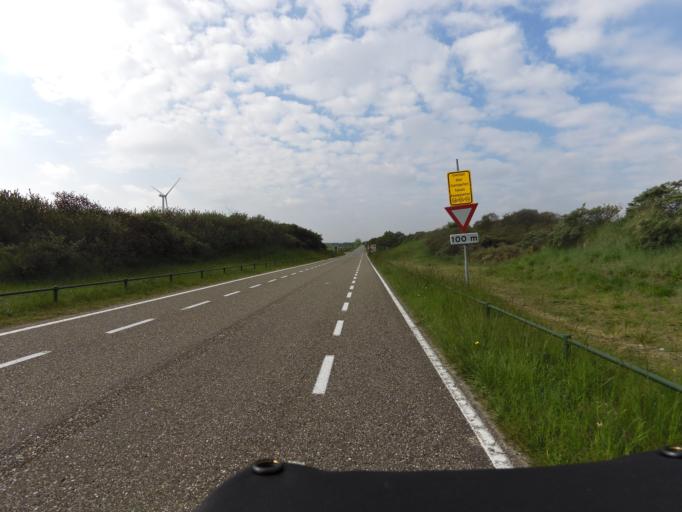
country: NL
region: Zeeland
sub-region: Gemeente Noord-Beveland
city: Kamperland
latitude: 51.5968
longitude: 3.6801
